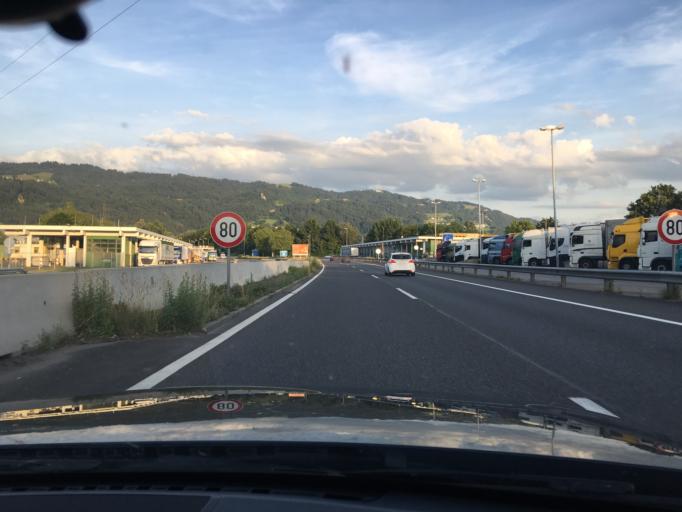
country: AT
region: Vorarlberg
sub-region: Politischer Bezirk Bregenz
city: Horbranz
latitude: 47.5463
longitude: 9.7369
